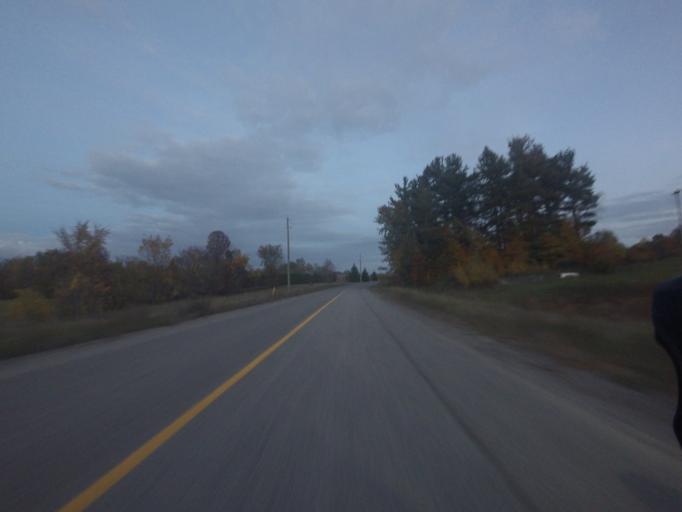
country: CA
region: Ontario
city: Renfrew
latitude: 45.3387
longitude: -76.9098
